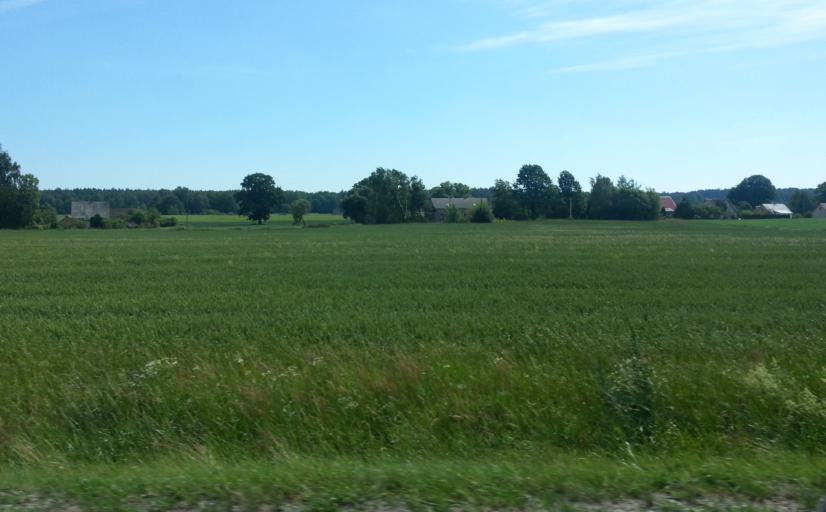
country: LT
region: Panevezys
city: Pasvalys
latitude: 55.9564
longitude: 24.3391
